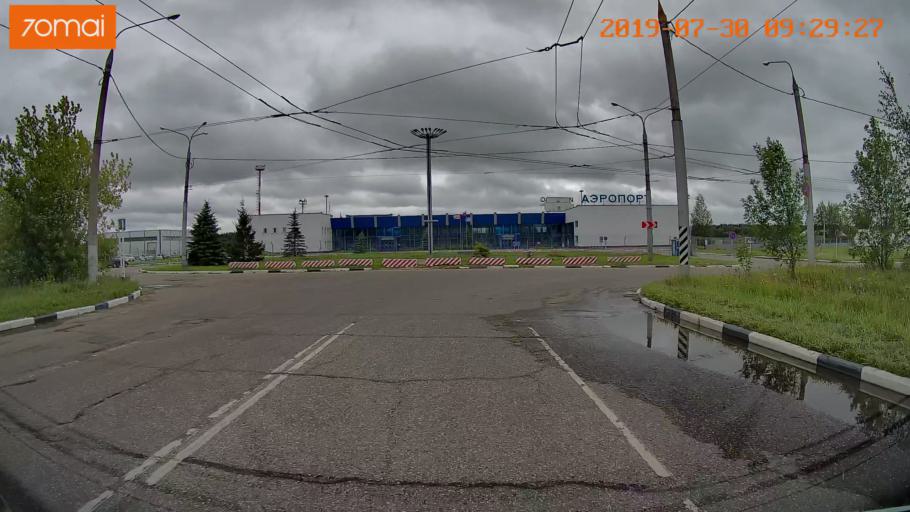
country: RU
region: Ivanovo
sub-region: Gorod Ivanovo
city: Ivanovo
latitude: 56.9434
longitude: 40.9449
